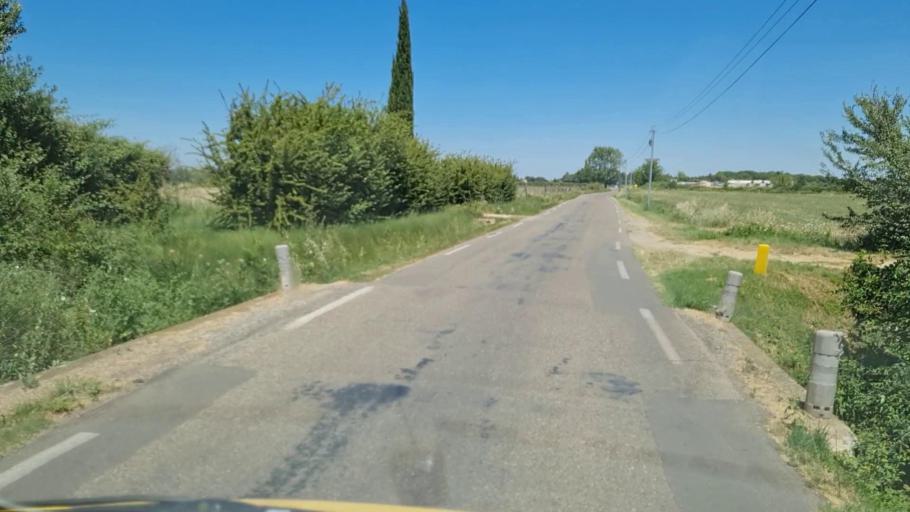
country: FR
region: Languedoc-Roussillon
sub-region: Departement du Gard
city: Aimargues
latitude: 43.6797
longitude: 4.1918
